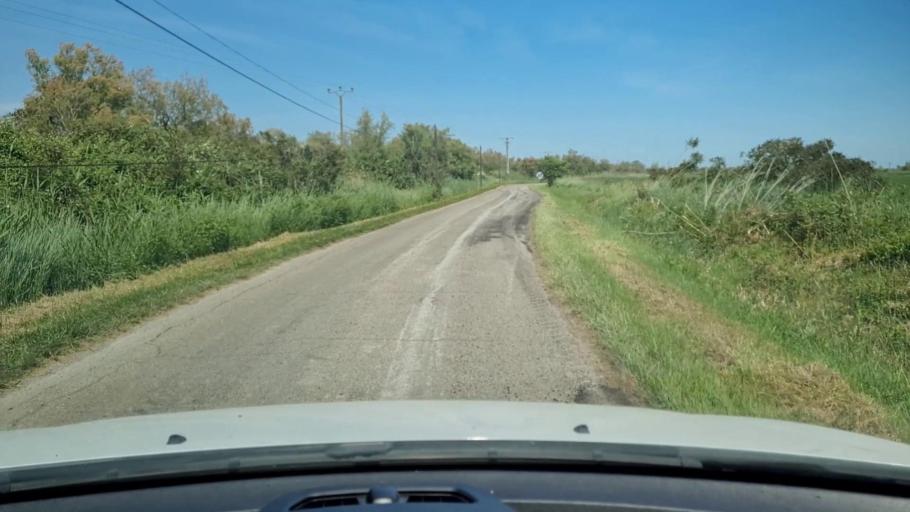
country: FR
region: Provence-Alpes-Cote d'Azur
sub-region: Departement des Bouches-du-Rhone
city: Saintes-Maries-de-la-Mer
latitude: 43.5637
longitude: 4.3832
